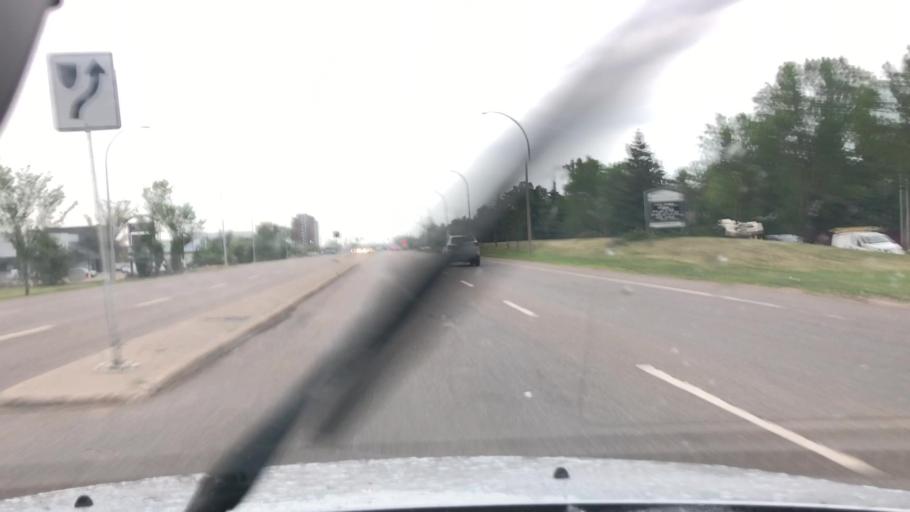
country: CA
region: Alberta
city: St. Albert
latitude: 53.5486
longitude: -113.6110
